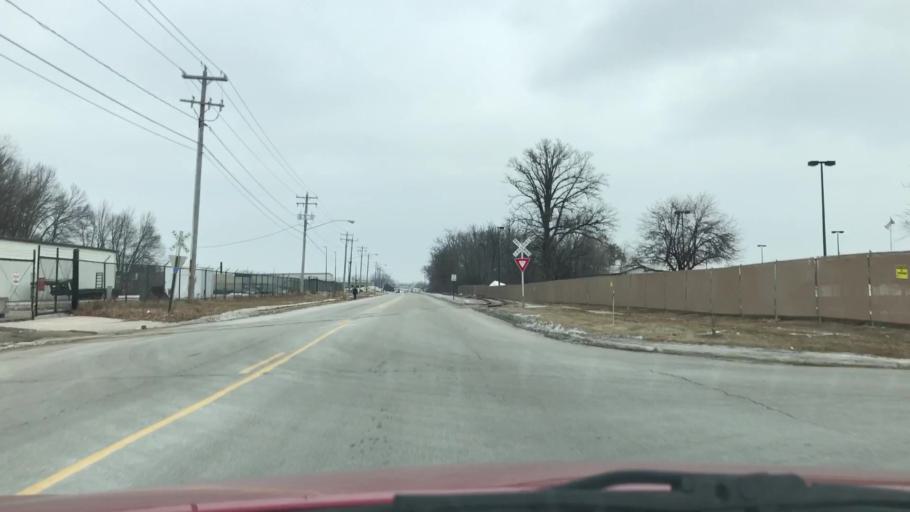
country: US
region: Wisconsin
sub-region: Brown County
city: Ashwaubenon
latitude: 44.4686
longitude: -88.0739
